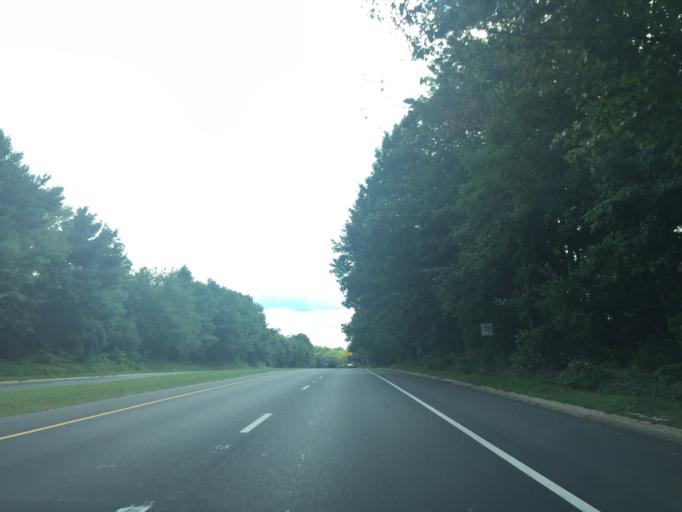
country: US
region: Maryland
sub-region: Montgomery County
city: Redland
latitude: 39.1426
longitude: -77.1573
